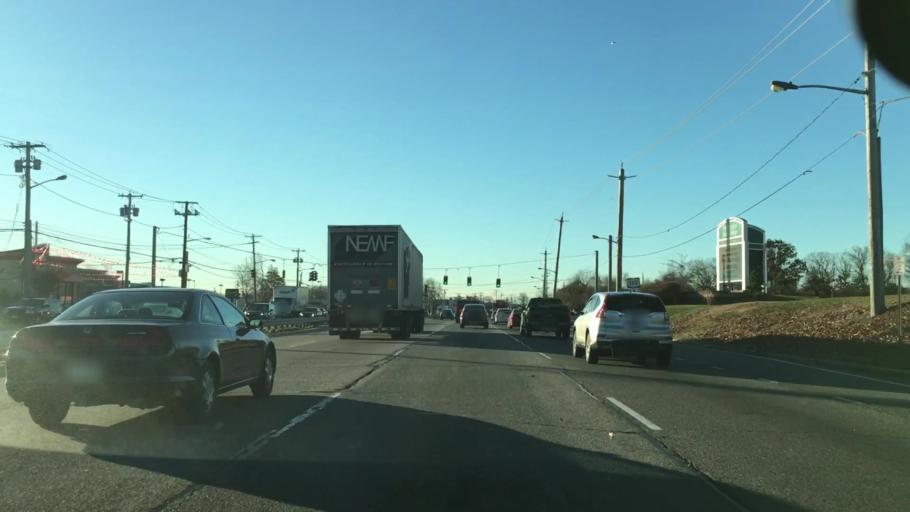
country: US
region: New York
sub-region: Suffolk County
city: East Farmingdale
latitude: 40.7512
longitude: -73.4222
